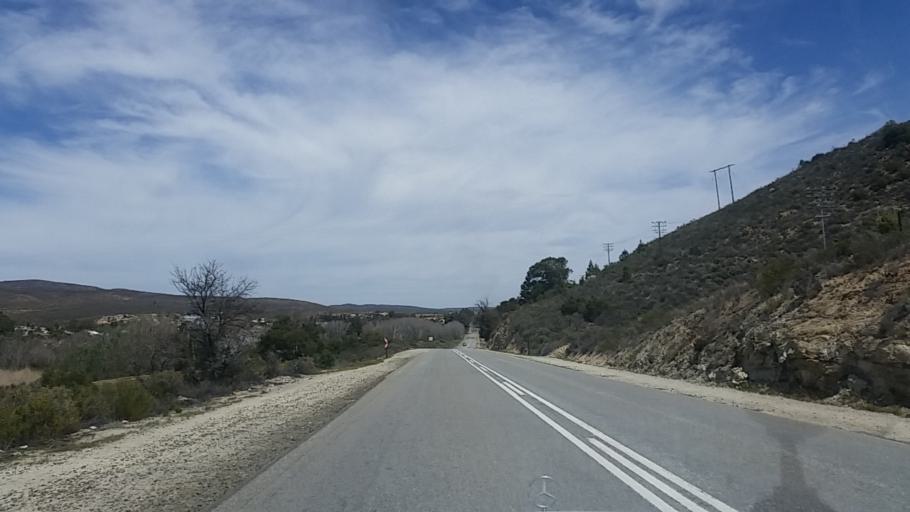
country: ZA
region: Western Cape
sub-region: Eden District Municipality
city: Knysna
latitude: -33.6490
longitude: 23.1290
